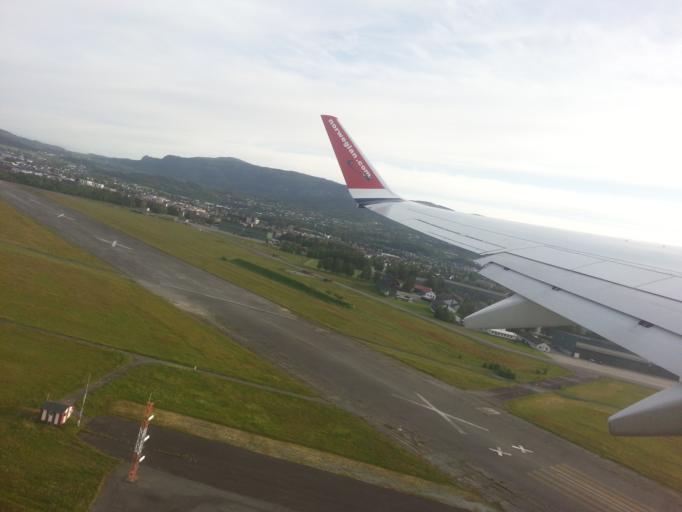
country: NO
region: Nord-Trondelag
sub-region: Stjordal
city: Stjordalshalsen
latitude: 63.4578
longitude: 10.9346
